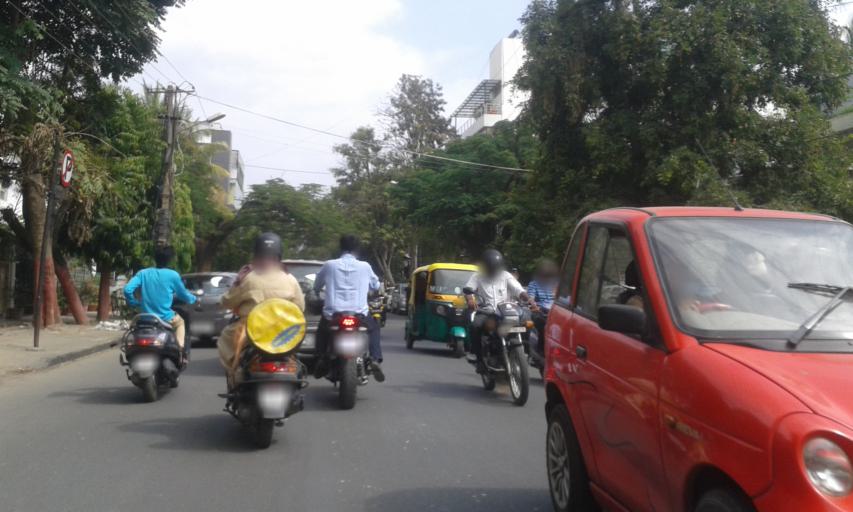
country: IN
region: Karnataka
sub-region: Bangalore Urban
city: Bangalore
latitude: 12.9703
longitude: 77.6425
